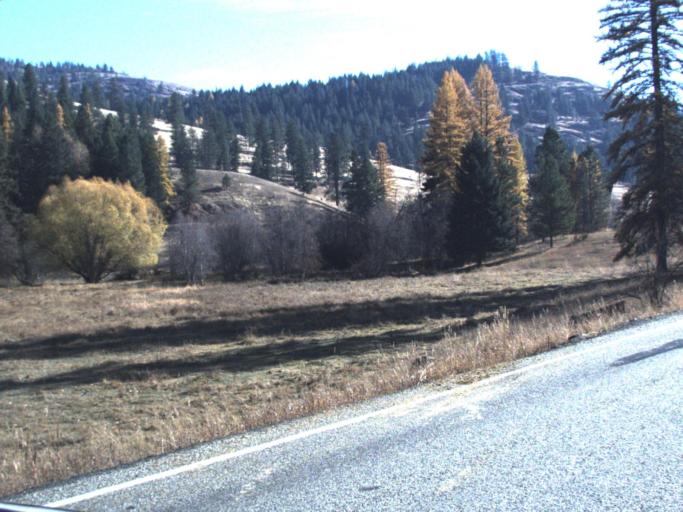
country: US
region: Washington
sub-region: Ferry County
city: Republic
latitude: 48.6111
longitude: -118.6623
